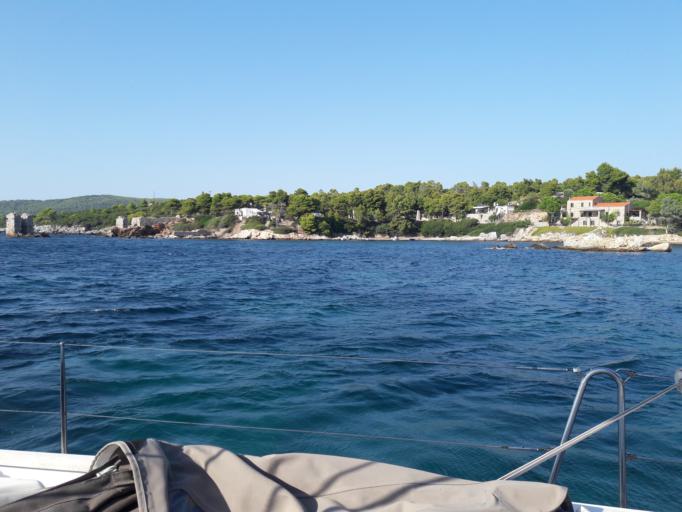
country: GR
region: Central Greece
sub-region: Nomos Evvoias
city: Skyros
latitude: 38.9157
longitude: 24.4660
